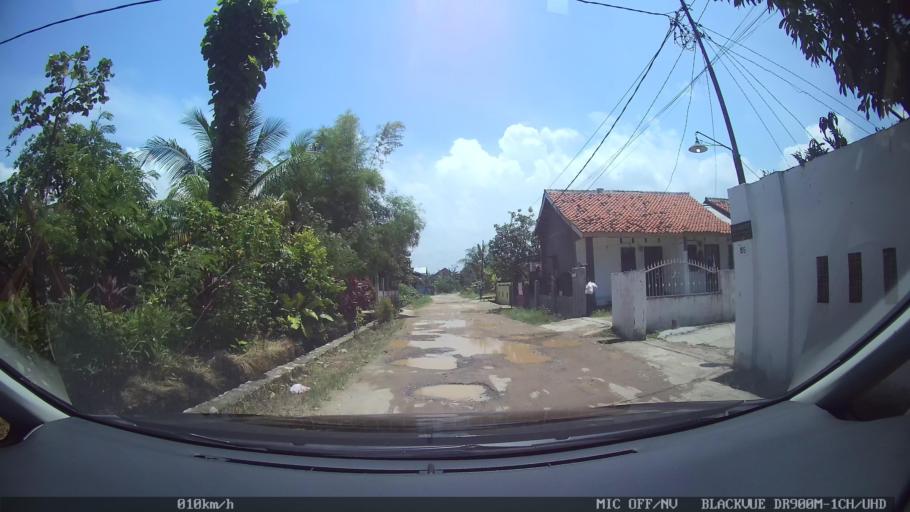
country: ID
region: Lampung
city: Kedaton
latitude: -5.3745
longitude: 105.2869
